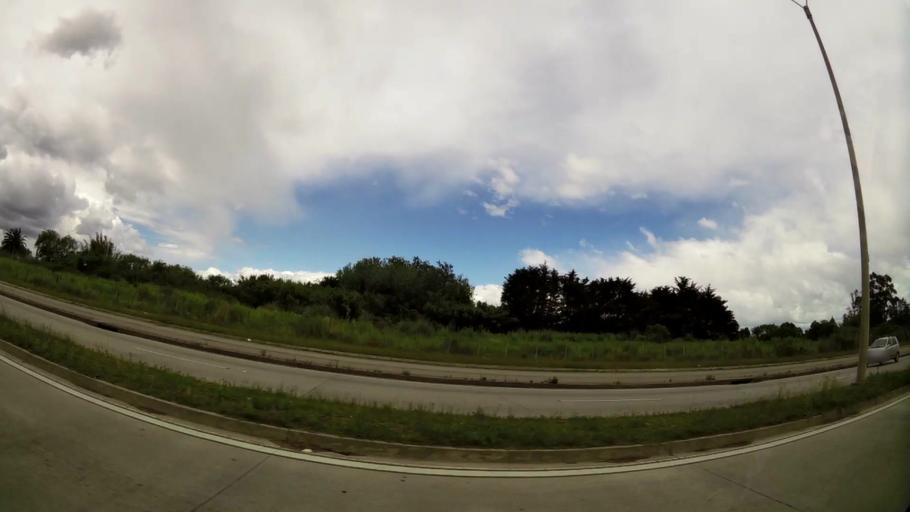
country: UY
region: Canelones
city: Toledo
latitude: -34.7955
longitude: -56.1338
